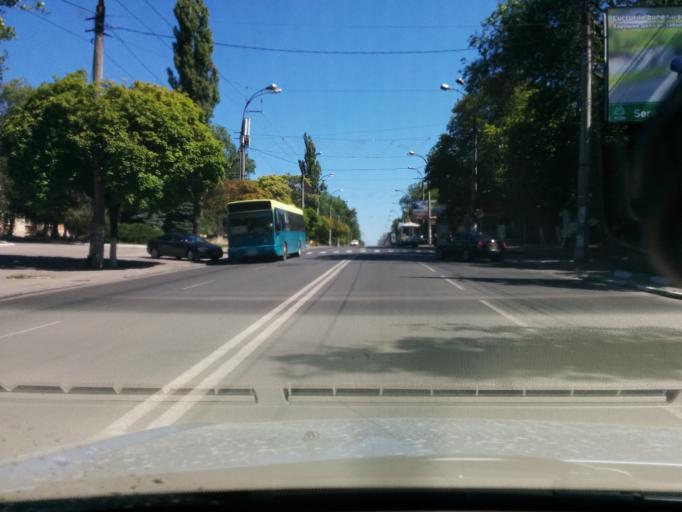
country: MD
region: Chisinau
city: Chisinau
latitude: 47.0396
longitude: 28.8595
